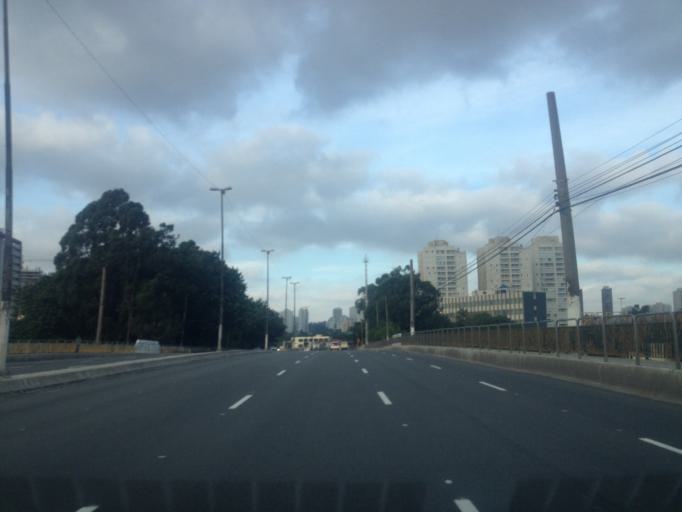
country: BR
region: Sao Paulo
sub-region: Taboao Da Serra
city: Taboao da Serra
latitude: -23.6655
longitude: -46.7108
